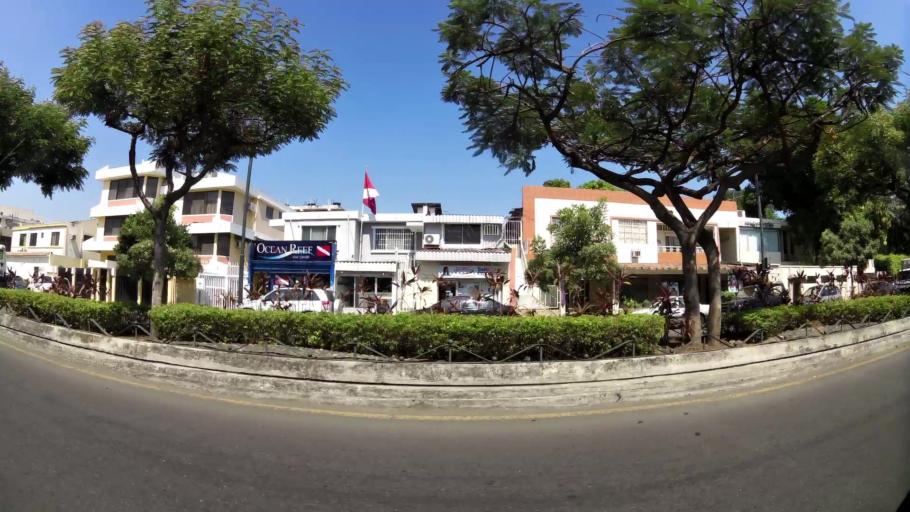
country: EC
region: Guayas
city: Guayaquil
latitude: -2.1618
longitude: -79.9184
